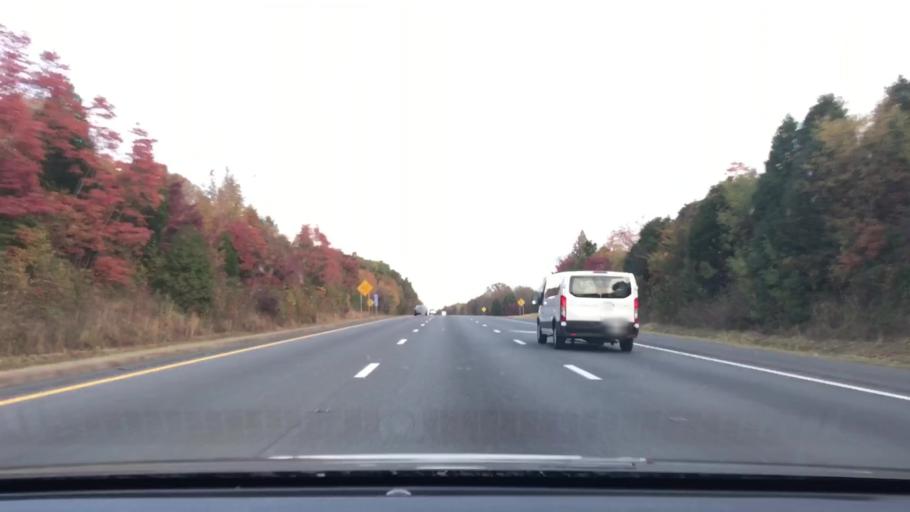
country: US
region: Tennessee
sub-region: Montgomery County
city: Clarksville
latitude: 36.5572
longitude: -87.2484
